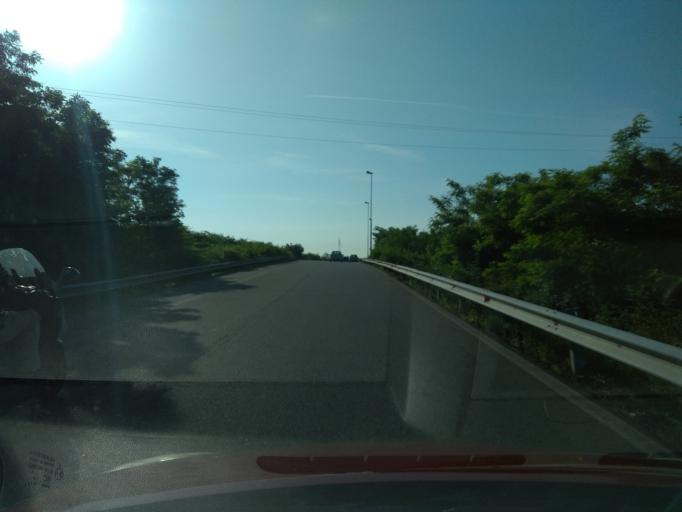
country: IT
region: Piedmont
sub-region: Provincia di Biella
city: Ronco Biellese
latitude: 45.5599
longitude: 8.0777
